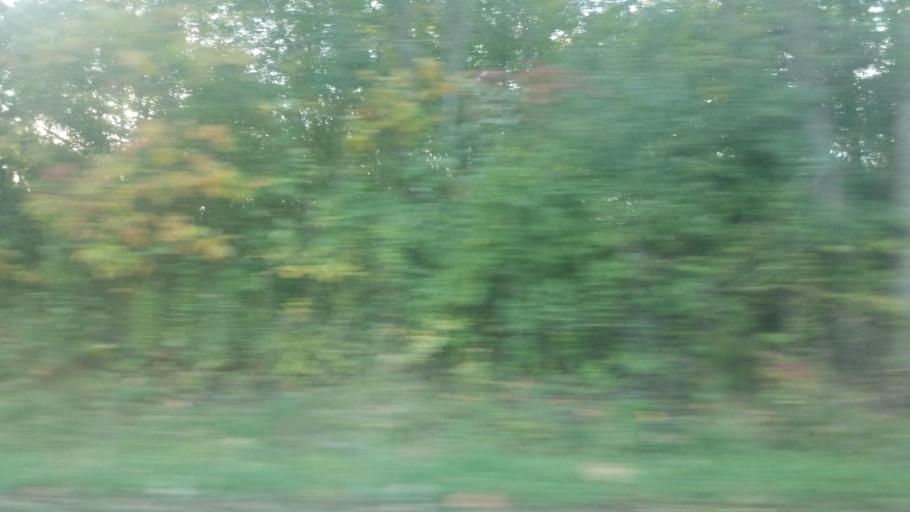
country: US
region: Illinois
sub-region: Williamson County
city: Marion
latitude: 37.7643
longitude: -88.8058
